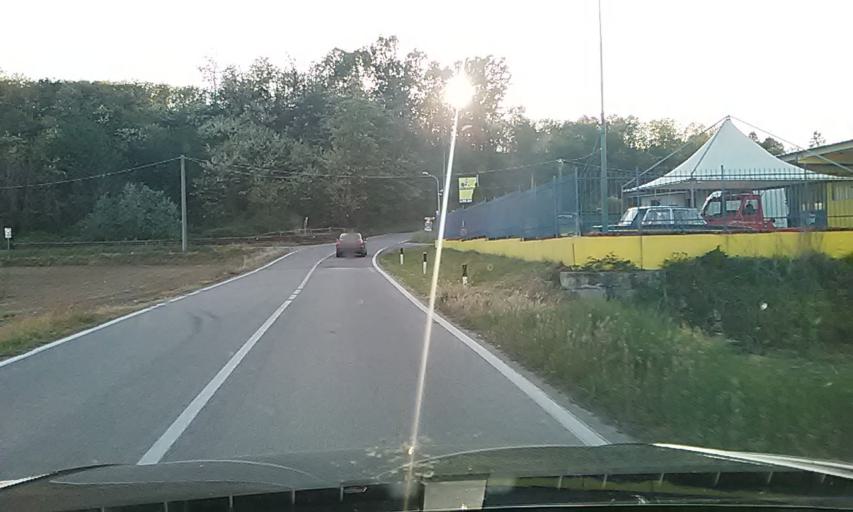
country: IT
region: Piedmont
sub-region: Provincia di Novara
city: Barengo
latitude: 45.5712
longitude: 8.5122
